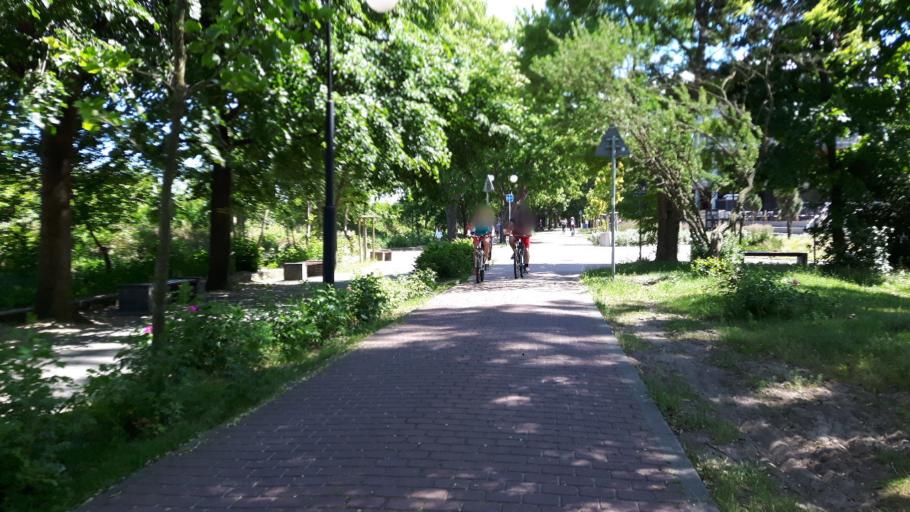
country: PL
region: Pomeranian Voivodeship
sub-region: Sopot
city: Sopot
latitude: 54.4348
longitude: 18.5835
